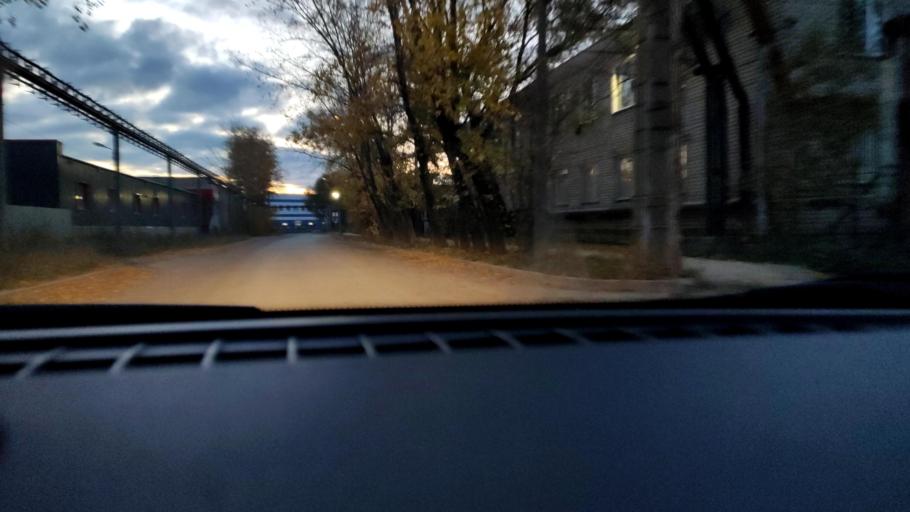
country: RU
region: Perm
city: Froly
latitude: 57.9634
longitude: 56.2597
